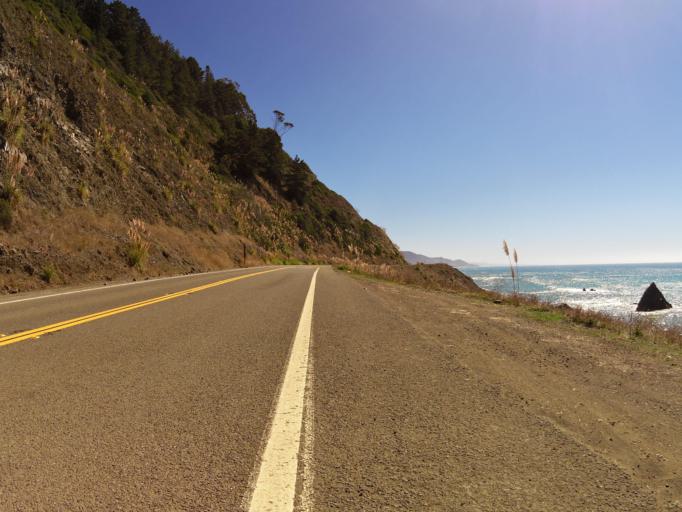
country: US
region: California
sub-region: Mendocino County
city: Fort Bragg
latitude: 39.7096
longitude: -123.8067
